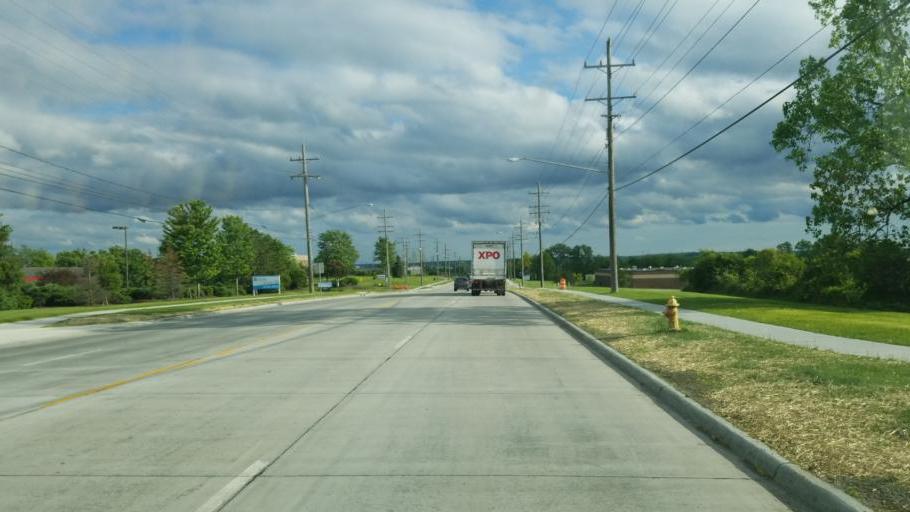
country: US
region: Ohio
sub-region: Cuyahoga County
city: Solon
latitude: 41.3789
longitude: -81.4693
